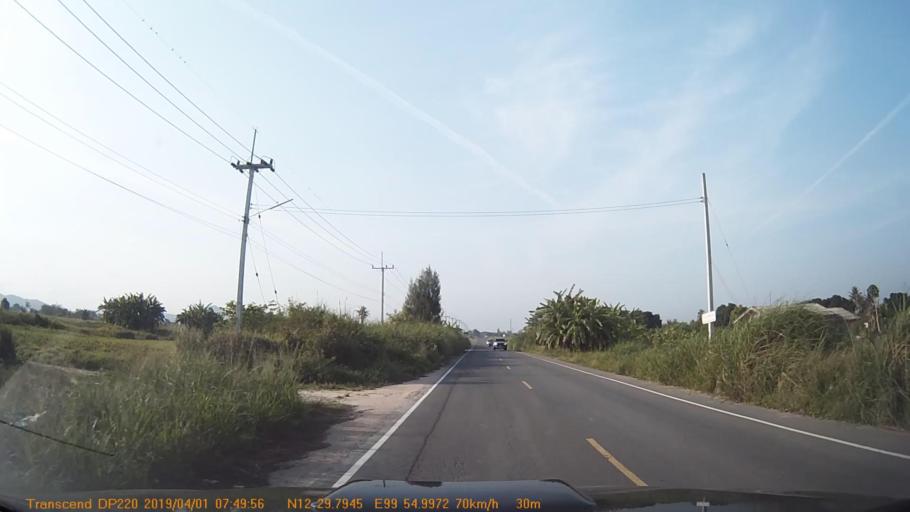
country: TH
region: Prachuap Khiri Khan
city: Hua Hin
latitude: 12.4964
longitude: 99.9166
